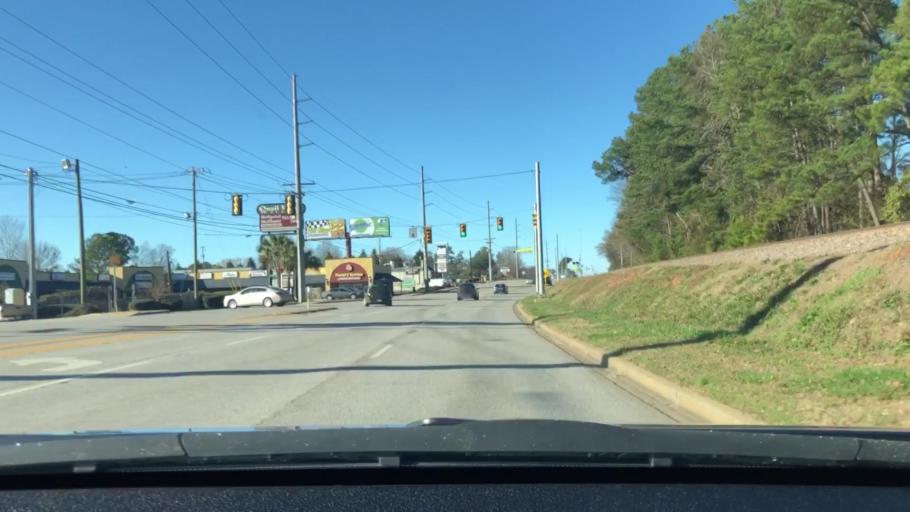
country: US
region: South Carolina
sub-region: Lexington County
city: Irmo
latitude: 34.0711
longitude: -81.1746
